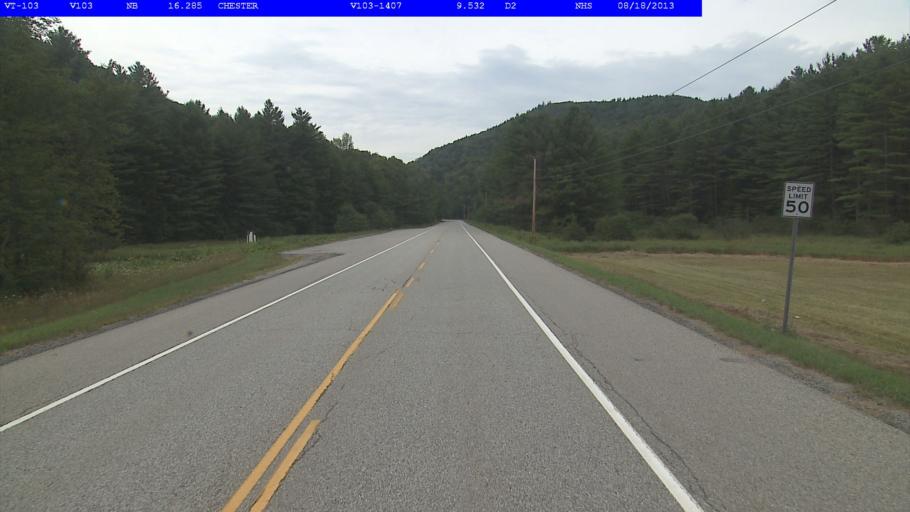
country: US
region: Vermont
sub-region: Windsor County
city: Chester
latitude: 43.3467
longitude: -72.6241
